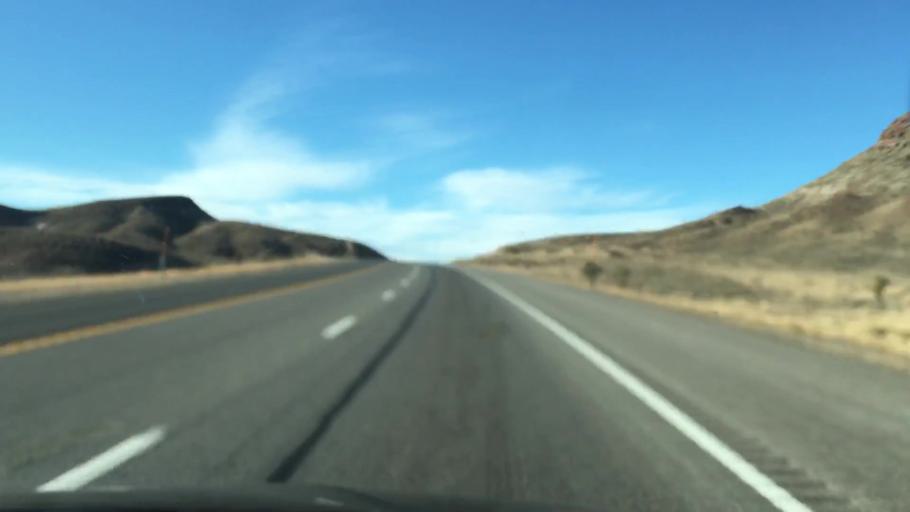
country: US
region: Nevada
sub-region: Esmeralda County
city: Goldfield
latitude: 37.6765
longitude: -117.2243
